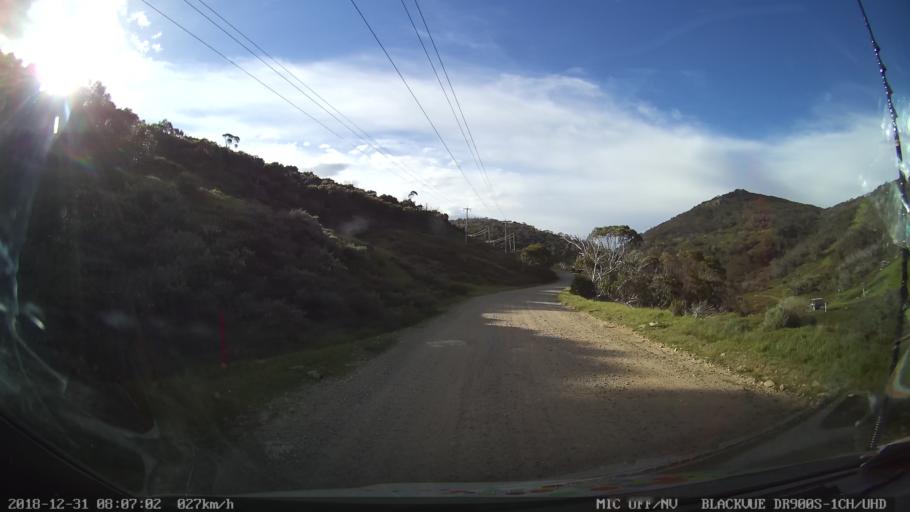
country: AU
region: New South Wales
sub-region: Snowy River
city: Jindabyne
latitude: -36.3769
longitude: 148.4088
